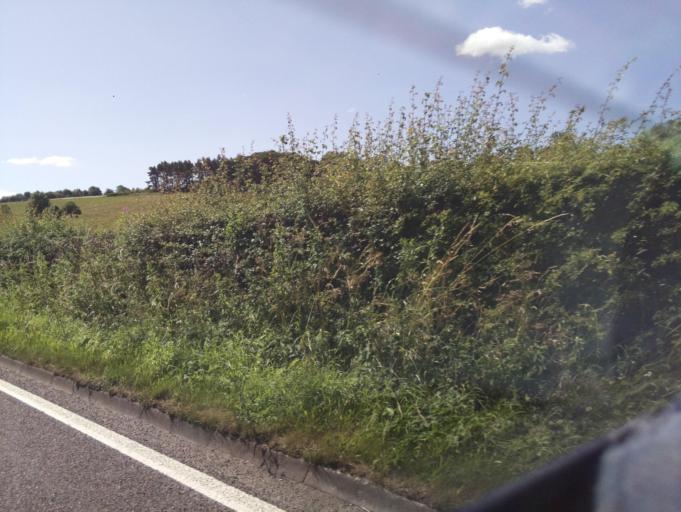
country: GB
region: England
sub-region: Derbyshire
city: Bakewell
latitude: 53.1979
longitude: -1.6601
